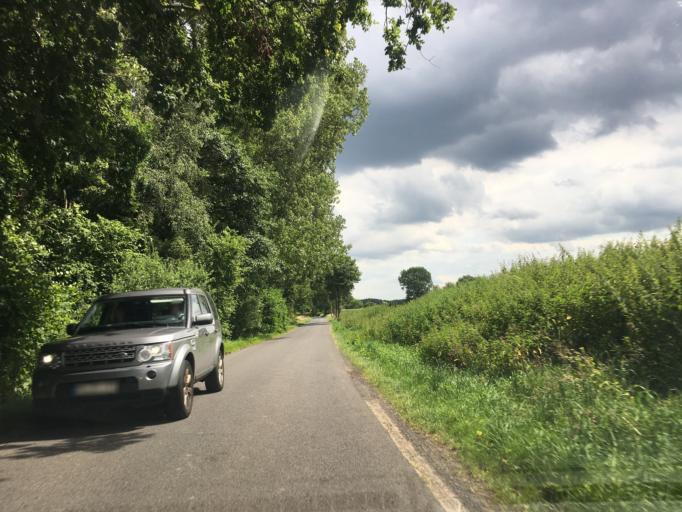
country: DE
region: North Rhine-Westphalia
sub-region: Regierungsbezirk Munster
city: Muenster
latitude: 51.9697
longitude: 7.6963
